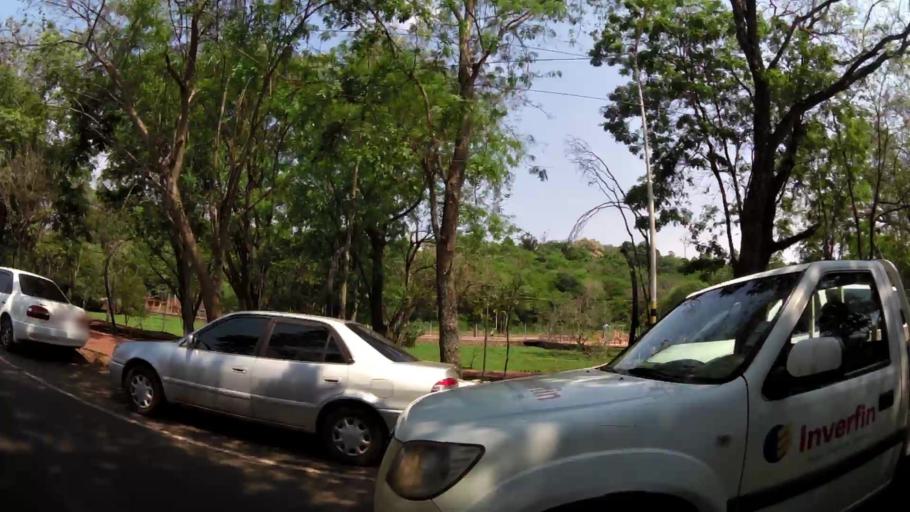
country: PY
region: Alto Parana
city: Presidente Franco
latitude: -25.5222
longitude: -54.6242
